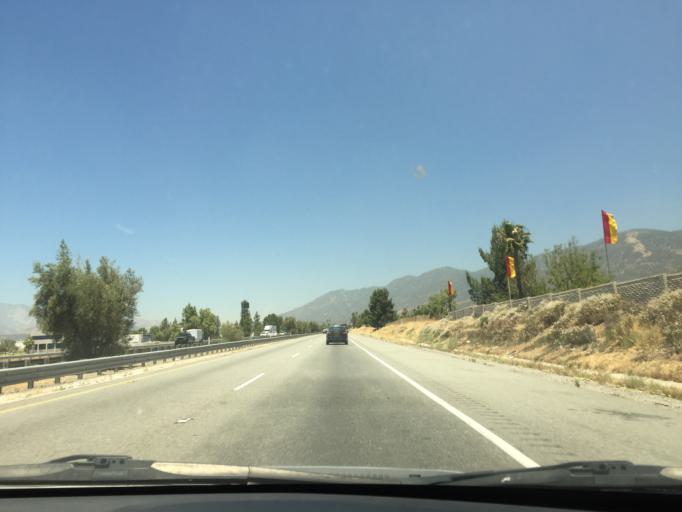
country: US
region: California
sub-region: San Bernardino County
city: Muscoy
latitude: 34.1716
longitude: -117.3393
